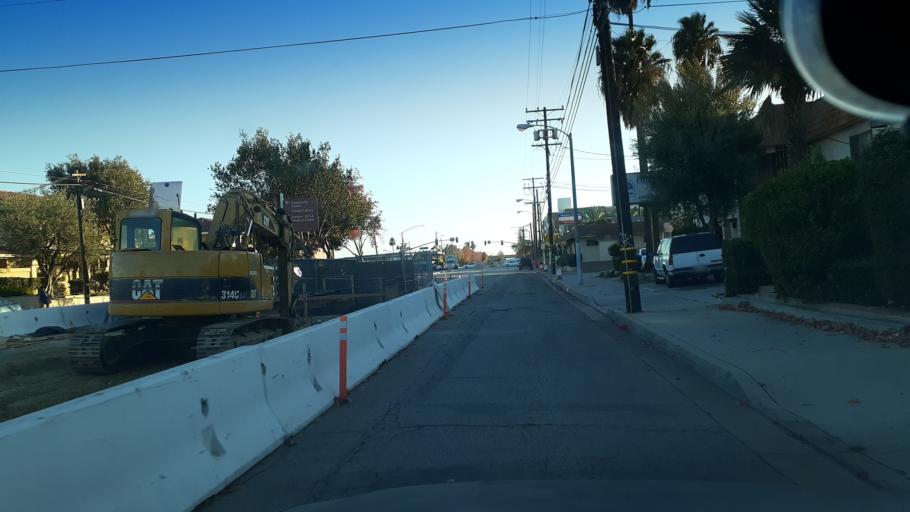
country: US
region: California
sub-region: Los Angeles County
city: Carson
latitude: 33.8332
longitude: -118.2862
